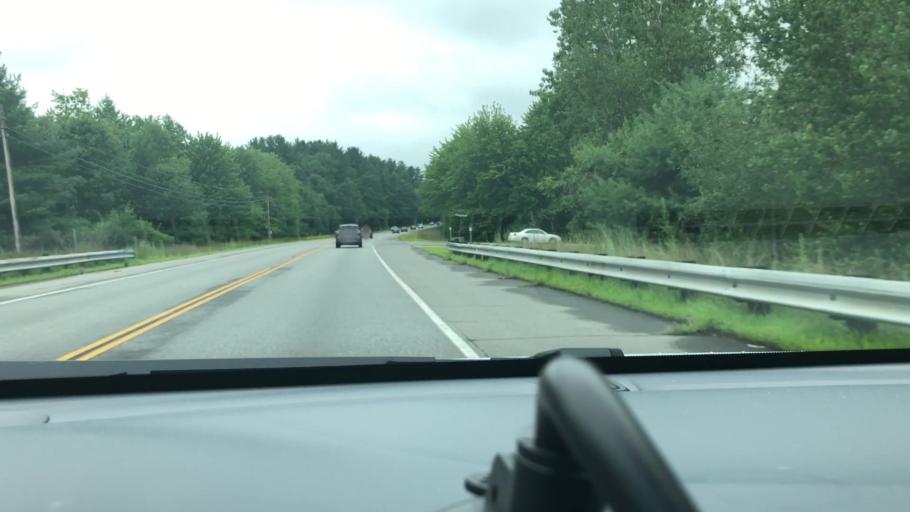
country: US
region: New Hampshire
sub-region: Hillsborough County
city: Pinardville
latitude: 42.9782
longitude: -71.5181
